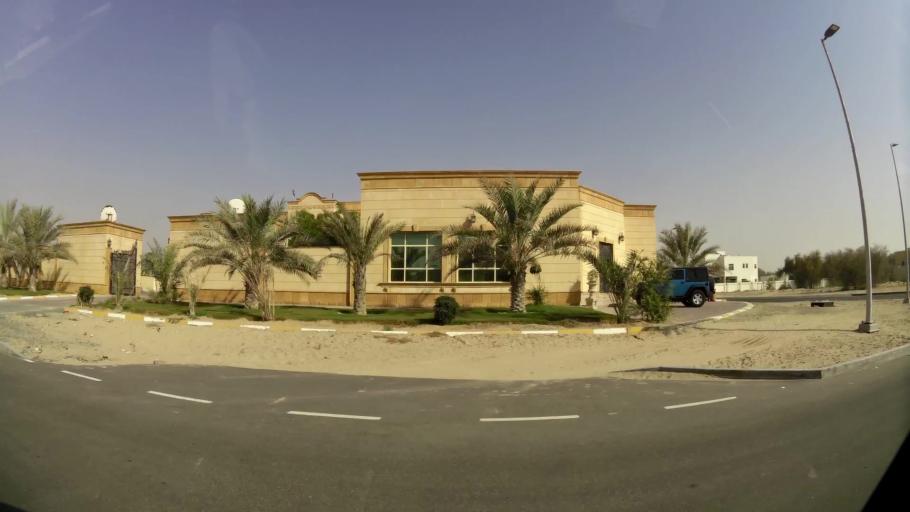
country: AE
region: Dubai
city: Dubai
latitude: 25.1500
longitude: 55.3175
